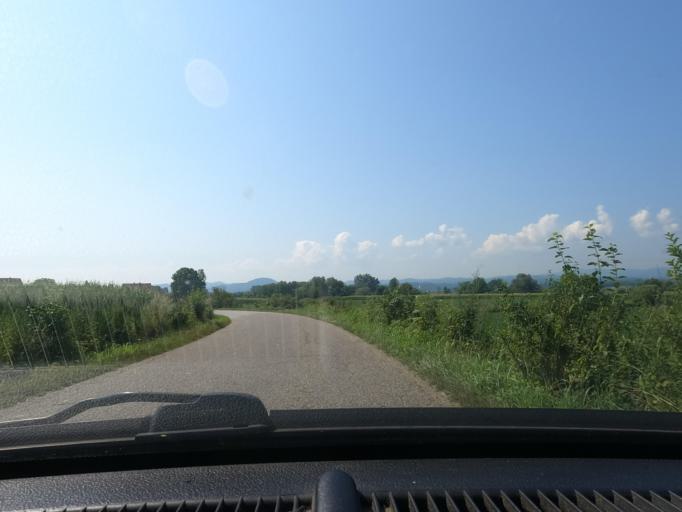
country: RS
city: Jarebice
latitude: 44.5383
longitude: 19.3710
